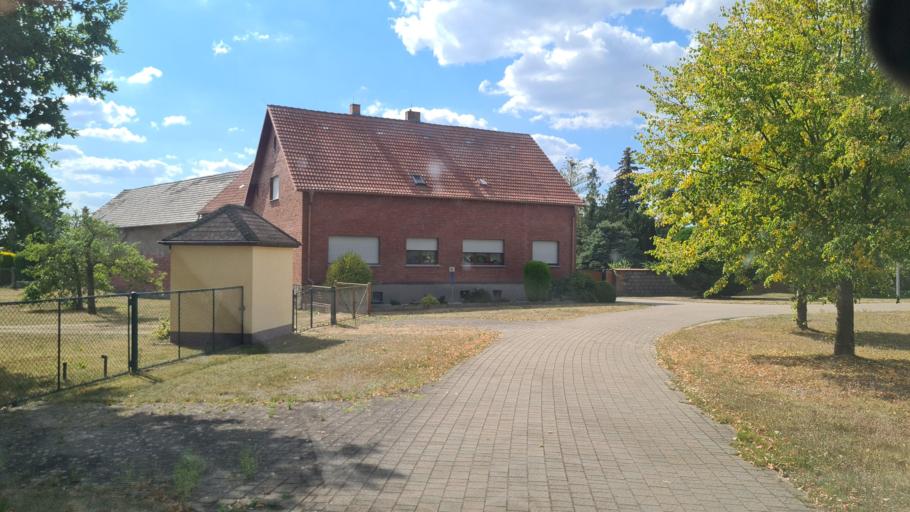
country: DE
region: Saxony-Anhalt
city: Elster
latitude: 51.8481
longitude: 12.8371
